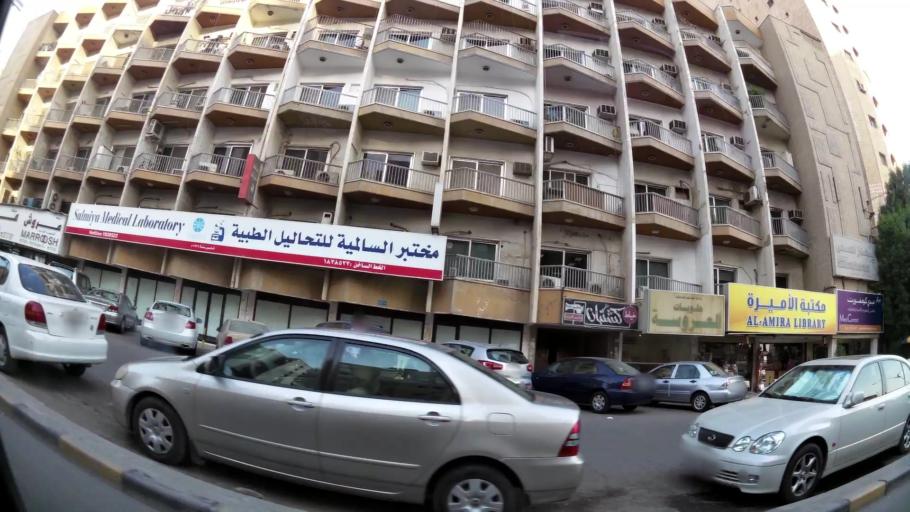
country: KW
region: Muhafazat Hawalli
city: As Salimiyah
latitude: 29.3341
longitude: 48.0540
